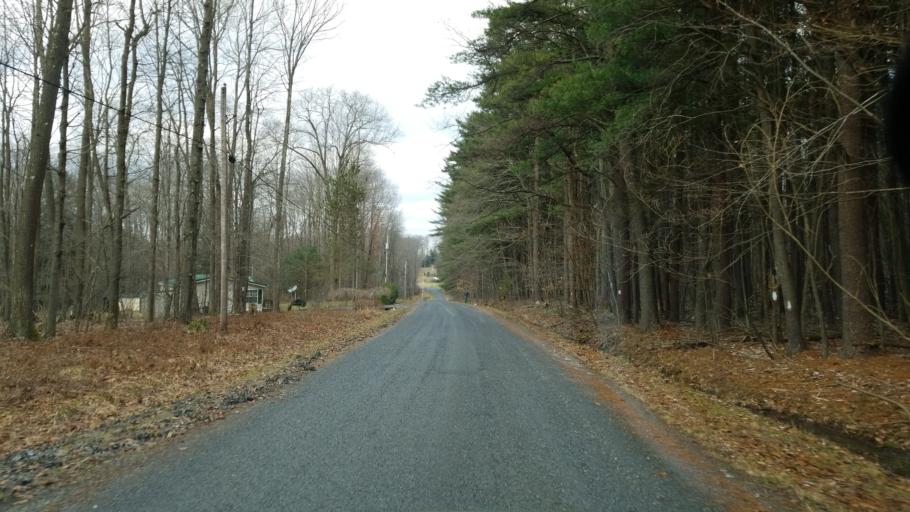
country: US
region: Pennsylvania
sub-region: Clearfield County
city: Clearfield
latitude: 41.1426
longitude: -78.5460
